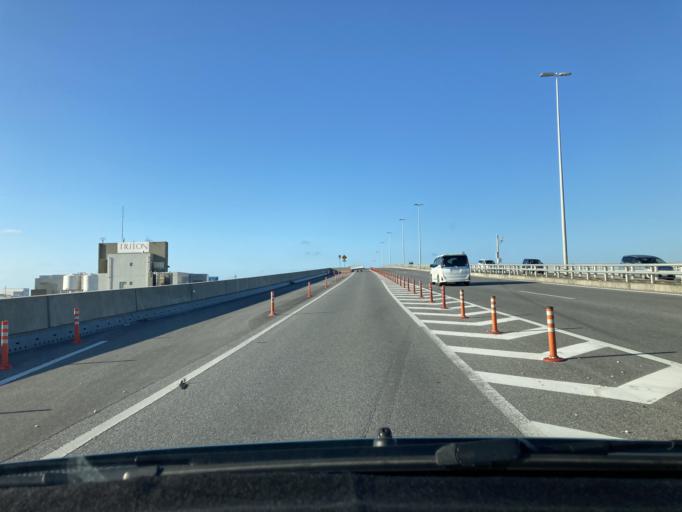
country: JP
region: Okinawa
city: Itoman
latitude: 26.1297
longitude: 127.6650
